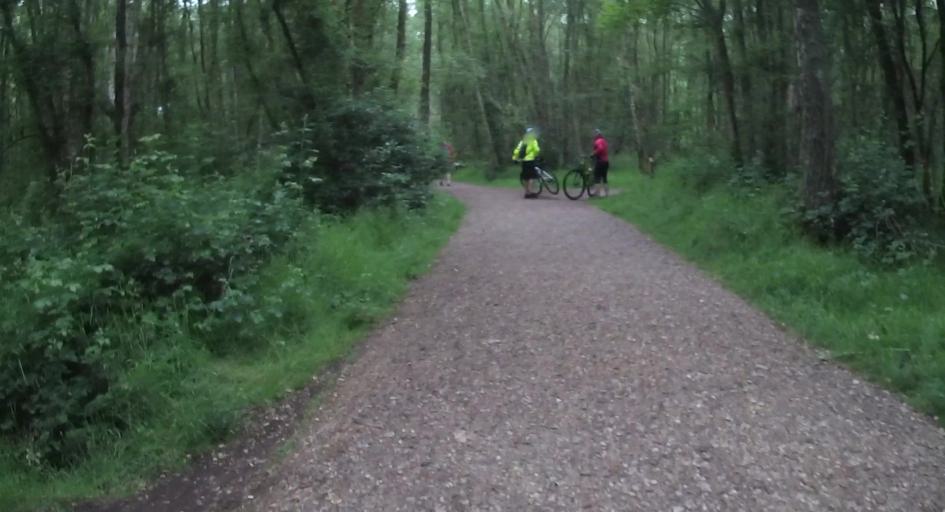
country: GB
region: England
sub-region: Hampshire
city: Farnborough
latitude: 51.2875
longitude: -0.7895
